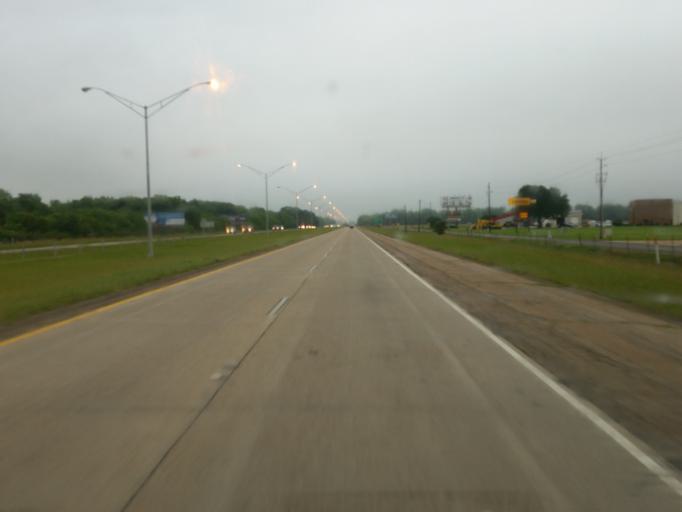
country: US
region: Louisiana
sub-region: Bossier Parish
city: Red Chute
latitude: 32.5329
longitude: -93.6568
